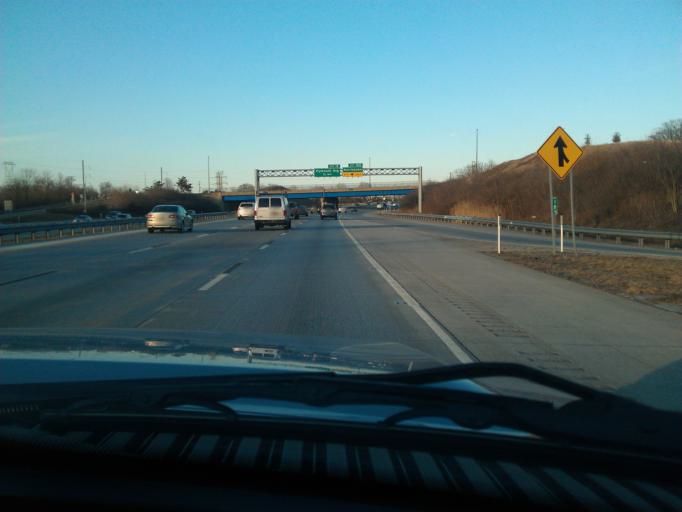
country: US
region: Pennsylvania
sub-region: Montgomery County
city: Conshohocken
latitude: 40.0959
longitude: -75.3025
